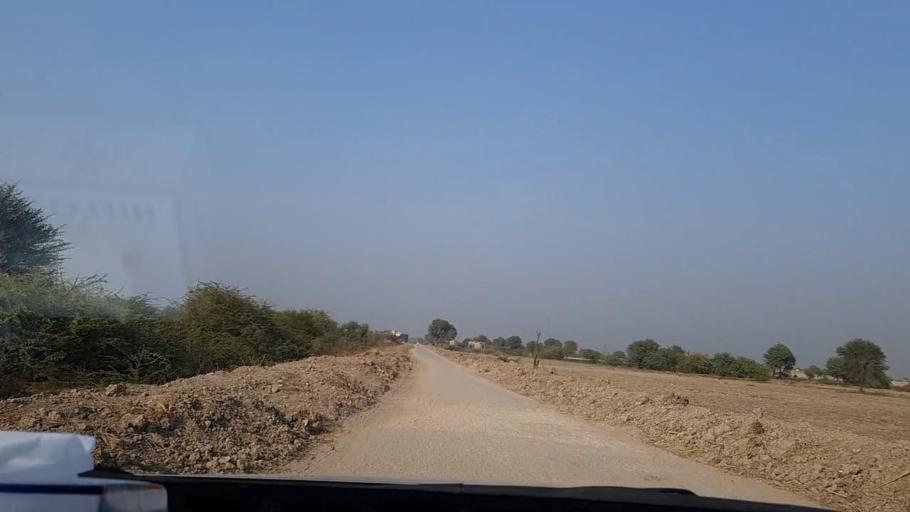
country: PK
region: Sindh
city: Tando Ghulam Ali
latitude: 25.2140
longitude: 68.8748
